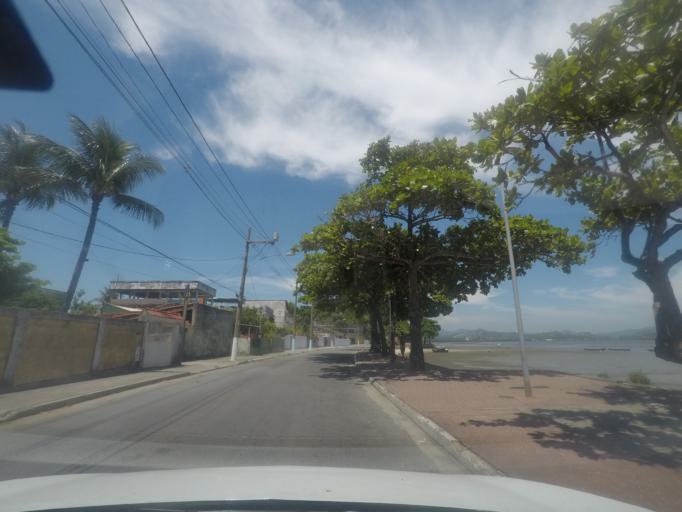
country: BR
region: Rio de Janeiro
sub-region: Itaguai
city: Itaguai
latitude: -22.9849
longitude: -43.6859
